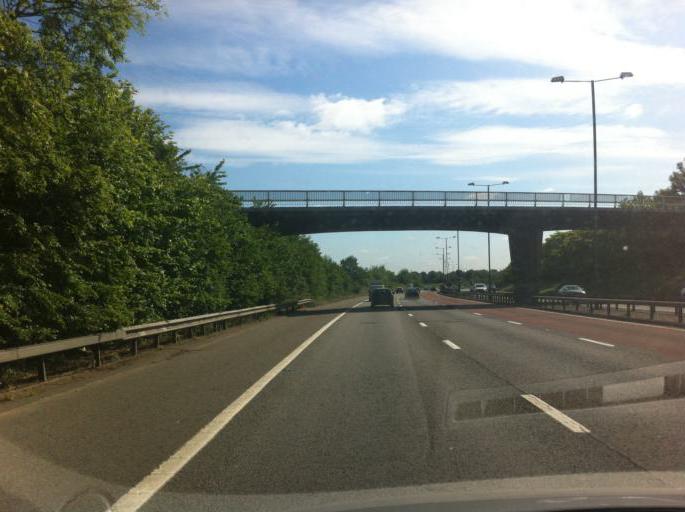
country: GB
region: England
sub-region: Greater London
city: Southall
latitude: 51.4905
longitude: -0.3660
